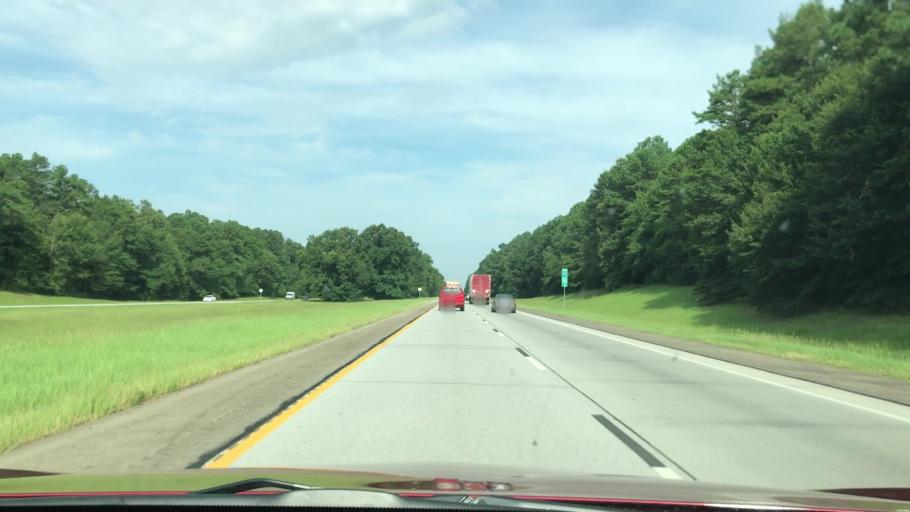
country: US
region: Georgia
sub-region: Columbia County
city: Appling
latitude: 33.5016
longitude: -82.3554
